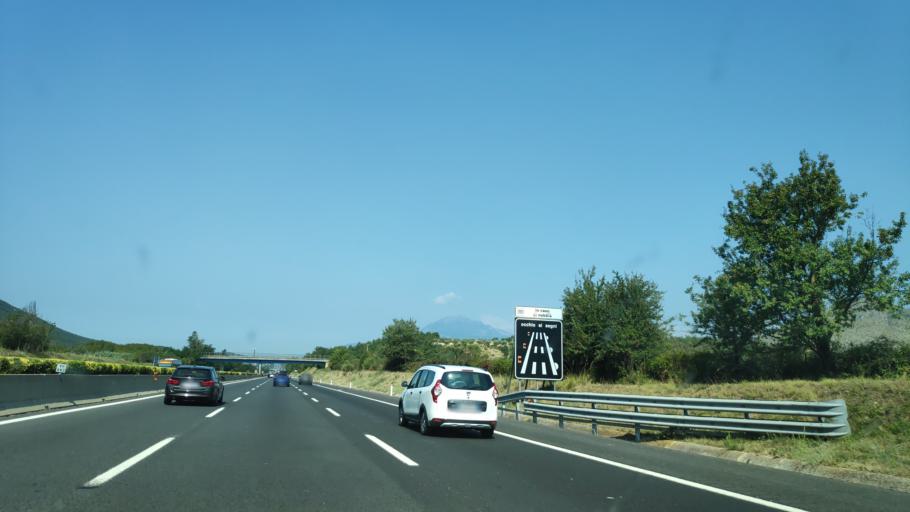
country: IT
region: Campania
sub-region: Provincia di Caserta
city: San Pietro Infine
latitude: 41.4129
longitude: 13.9489
